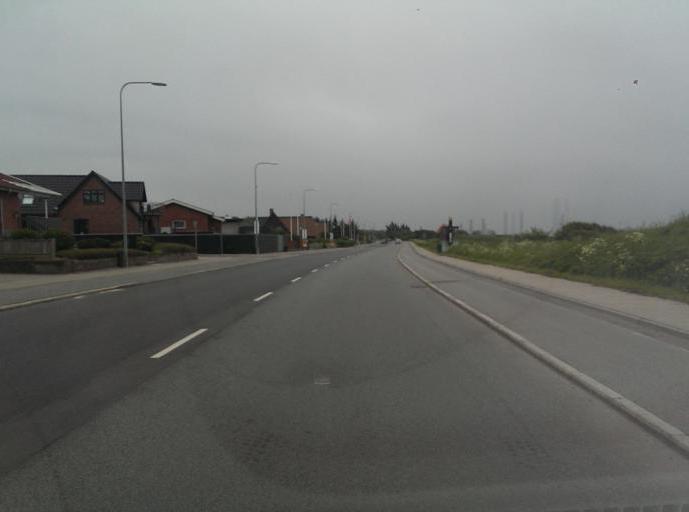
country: DK
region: South Denmark
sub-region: Fano Kommune
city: Nordby
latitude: 55.4981
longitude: 8.3952
